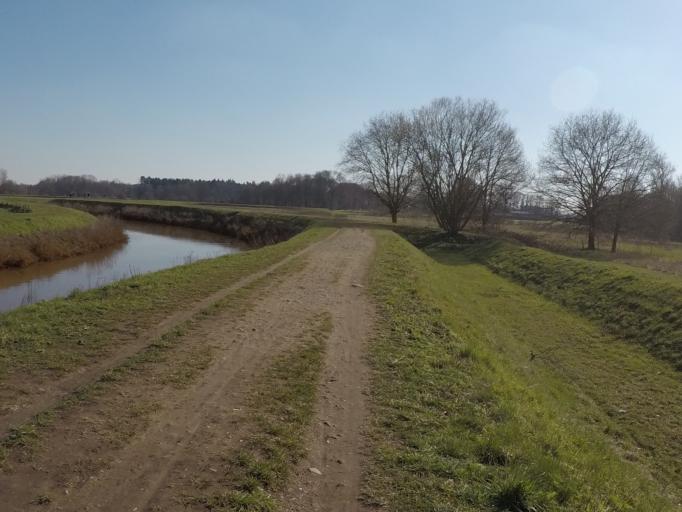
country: BE
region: Flanders
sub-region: Provincie Antwerpen
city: Herenthout
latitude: 51.1251
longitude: 4.7185
